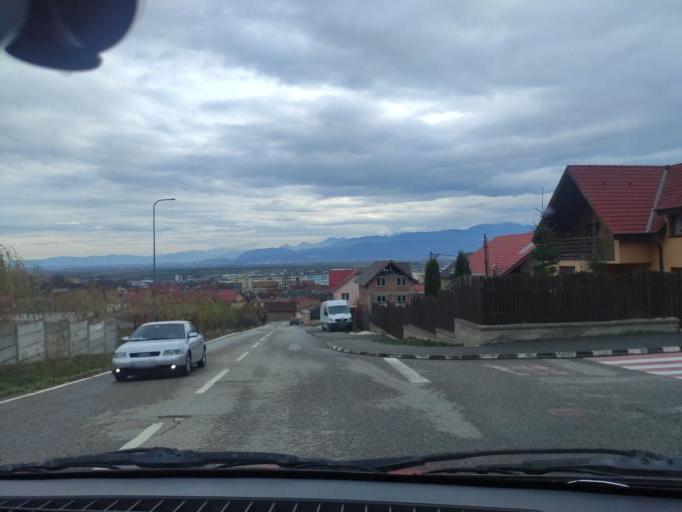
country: RO
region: Brasov
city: Codlea
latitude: 45.7078
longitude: 25.4438
